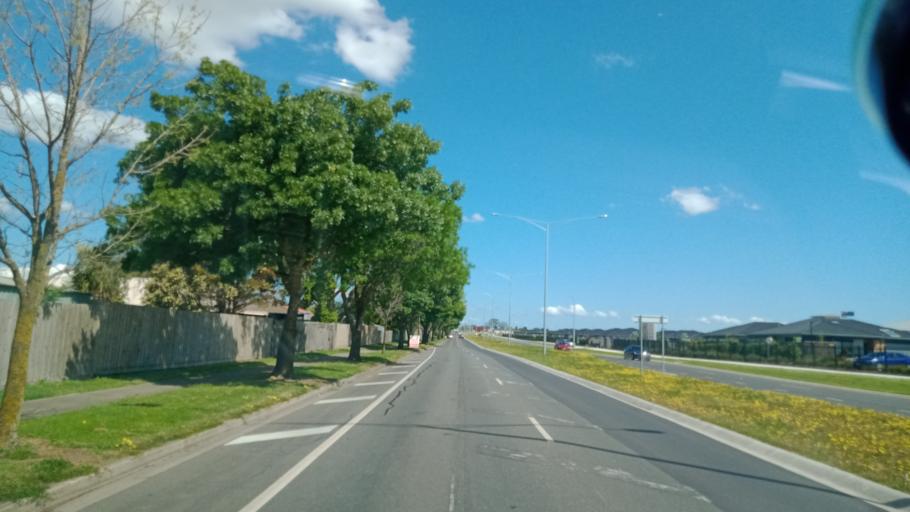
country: AU
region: Victoria
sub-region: Casey
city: Cranbourne West
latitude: -38.1030
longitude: 145.2537
